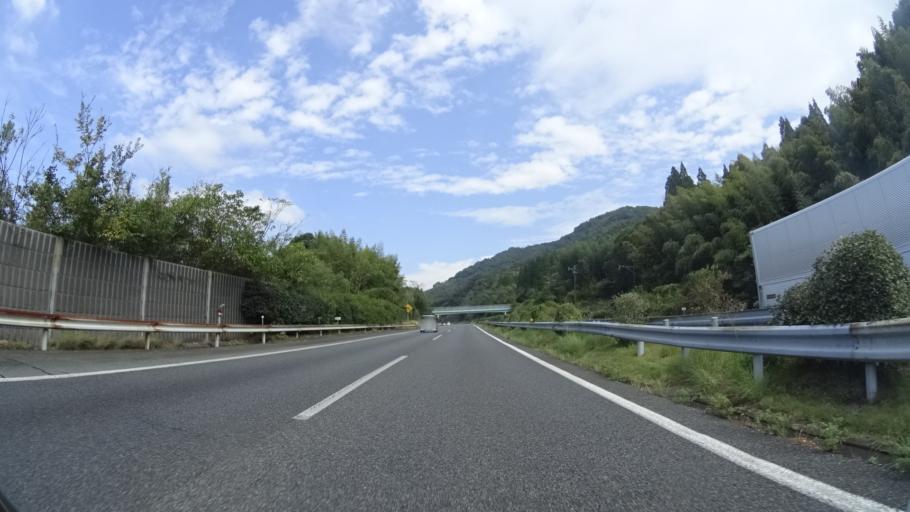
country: JP
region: Kumamoto
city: Matsubase
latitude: 32.6062
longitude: 130.7223
